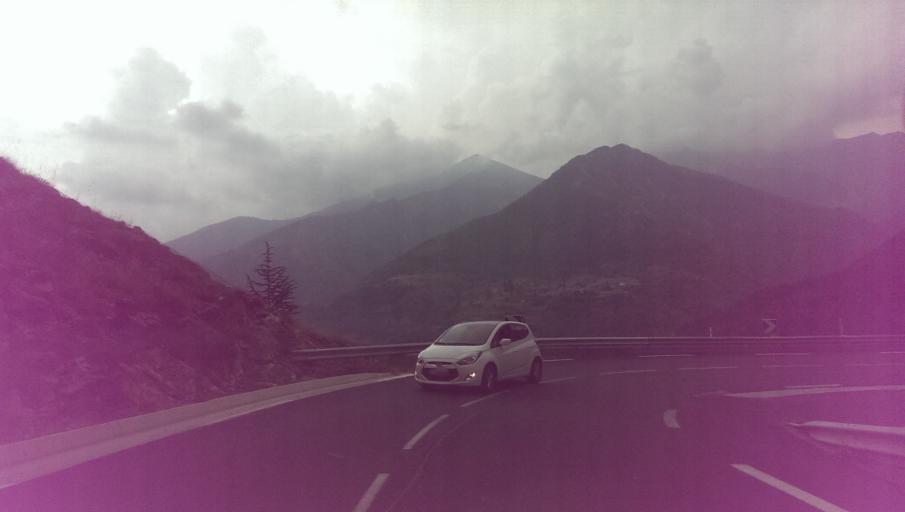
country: ES
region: Catalonia
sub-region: Provincia de Girona
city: Llivia
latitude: 42.5071
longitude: 2.1587
